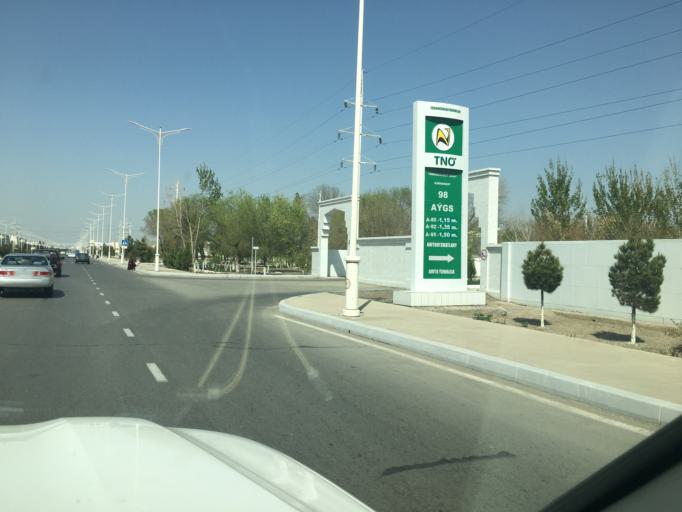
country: TM
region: Lebap
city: Turkmenabat
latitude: 39.0390
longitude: 63.5886
